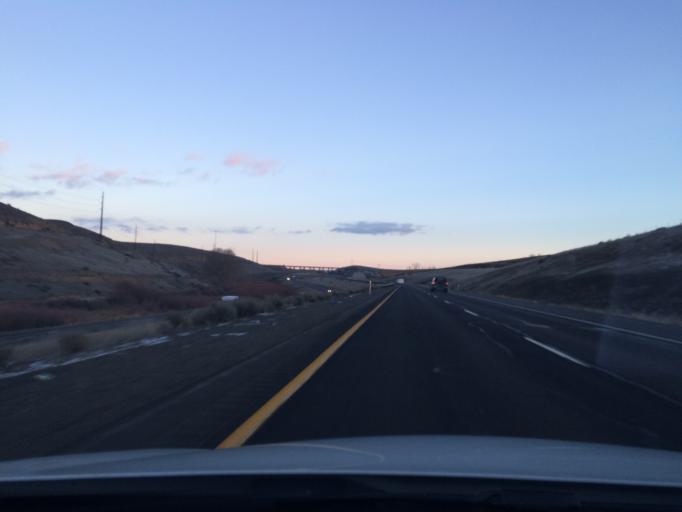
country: US
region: Washington
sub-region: Kittitas County
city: Kittitas
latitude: 46.9598
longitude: -120.3236
